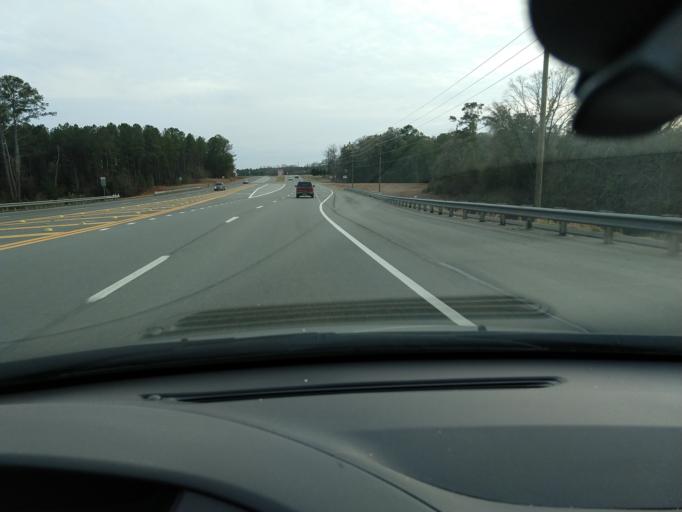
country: US
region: Georgia
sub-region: Sumter County
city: Americus
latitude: 32.0605
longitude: -84.2530
